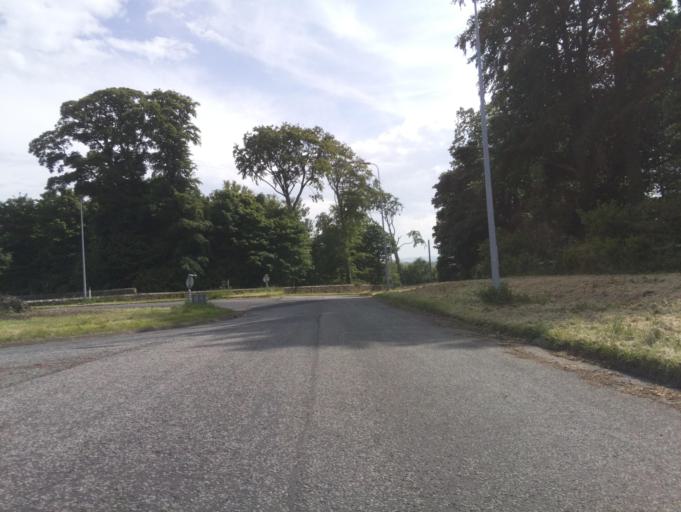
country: GB
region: England
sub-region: Northumberland
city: Alnwick
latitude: 55.4273
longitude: -1.7008
